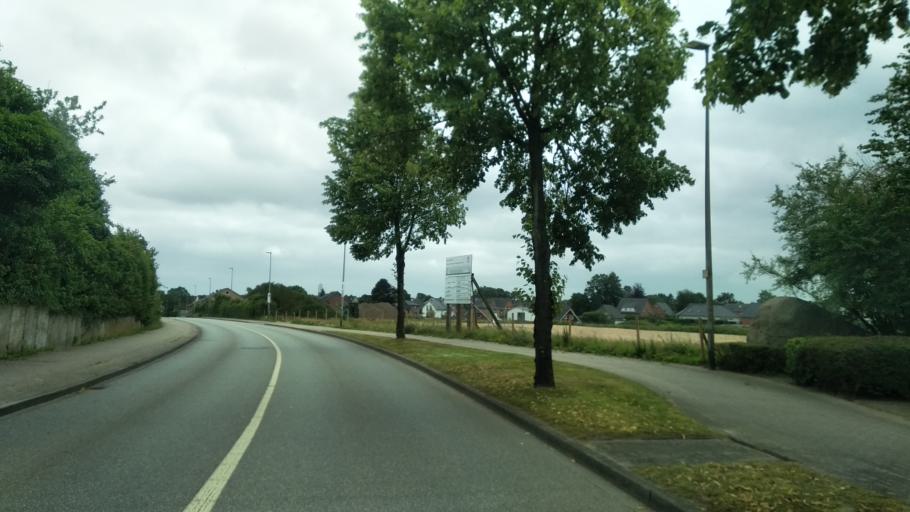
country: DE
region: Schleswig-Holstein
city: Schleswig
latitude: 54.5324
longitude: 9.5564
